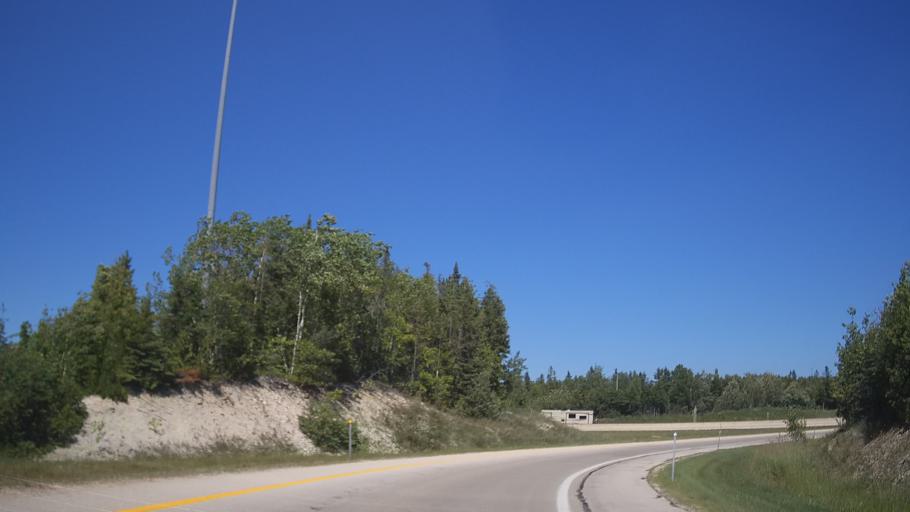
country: US
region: Michigan
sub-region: Mackinac County
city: Saint Ignace
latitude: 45.8588
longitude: -84.7314
